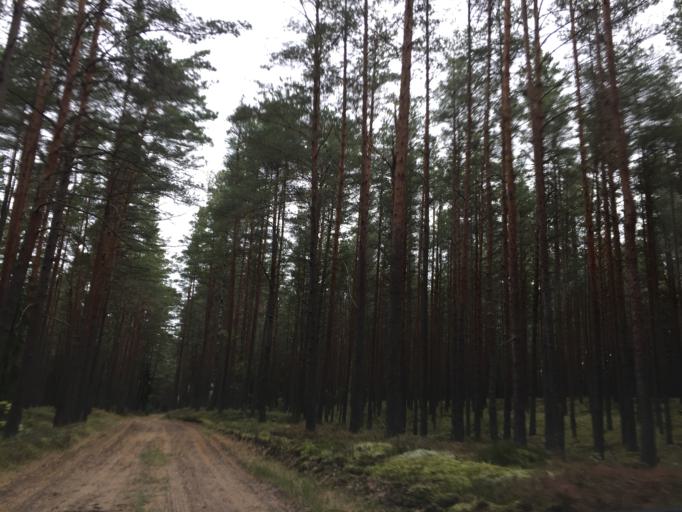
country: LV
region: Salacgrivas
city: Salacgriva
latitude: 57.7085
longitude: 24.3528
